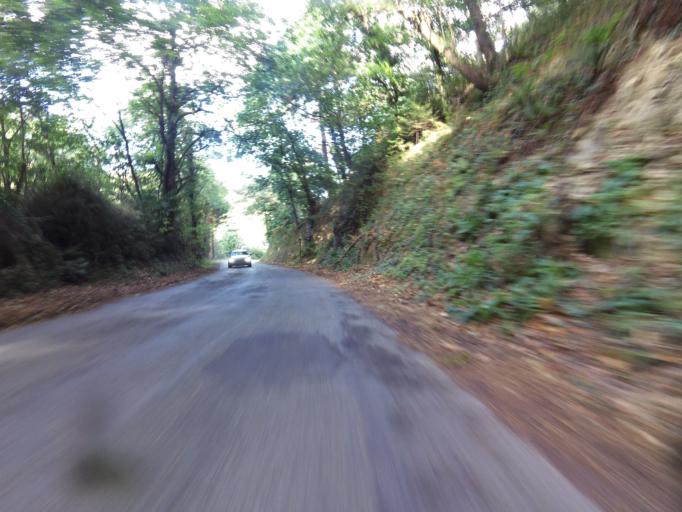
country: FR
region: Brittany
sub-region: Departement des Cotes-d'Armor
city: Plouha
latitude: 48.6749
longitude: -2.8882
